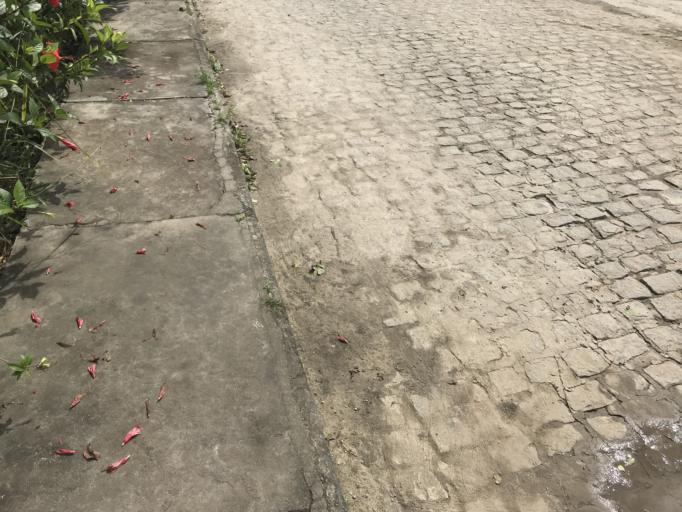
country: BR
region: Bahia
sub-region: Santo Antonio De Jesus
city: Santo Antonio de Jesus
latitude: -12.9804
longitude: -39.2823
